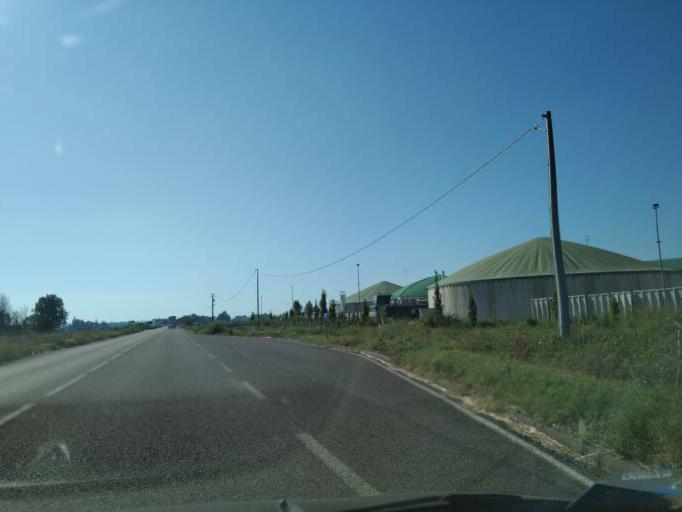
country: IT
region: Emilia-Romagna
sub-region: Provincia di Modena
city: Nonantola
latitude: 44.6771
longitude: 11.0785
